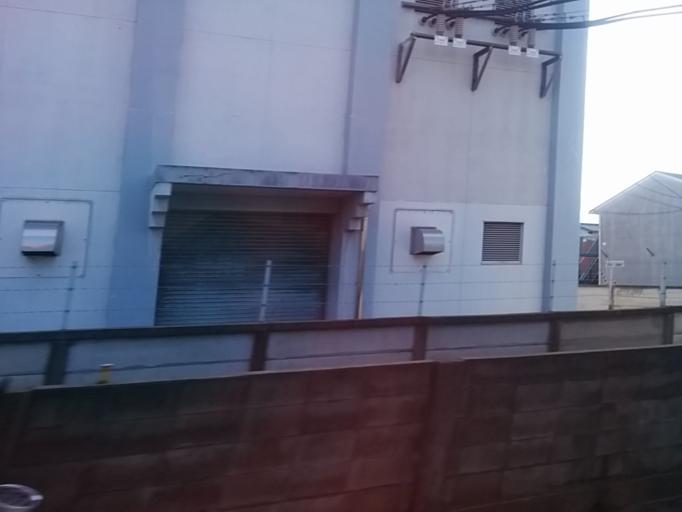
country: JP
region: Nara
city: Nara-shi
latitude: 34.7383
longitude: 135.7941
